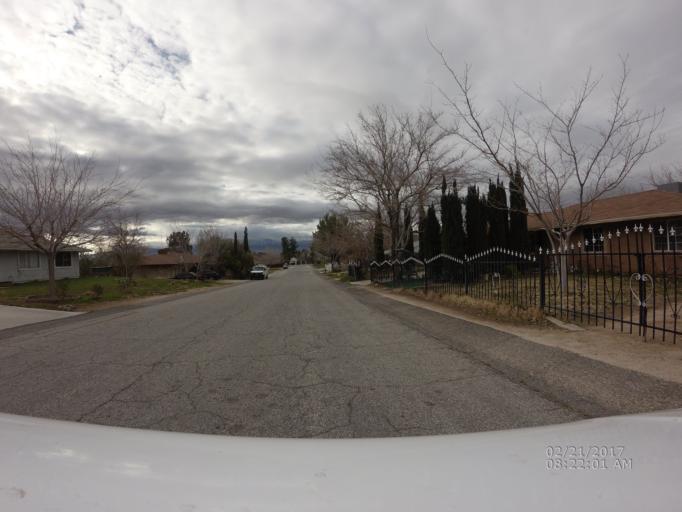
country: US
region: California
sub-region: Los Angeles County
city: Lake Los Angeles
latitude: 34.5995
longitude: -117.8403
